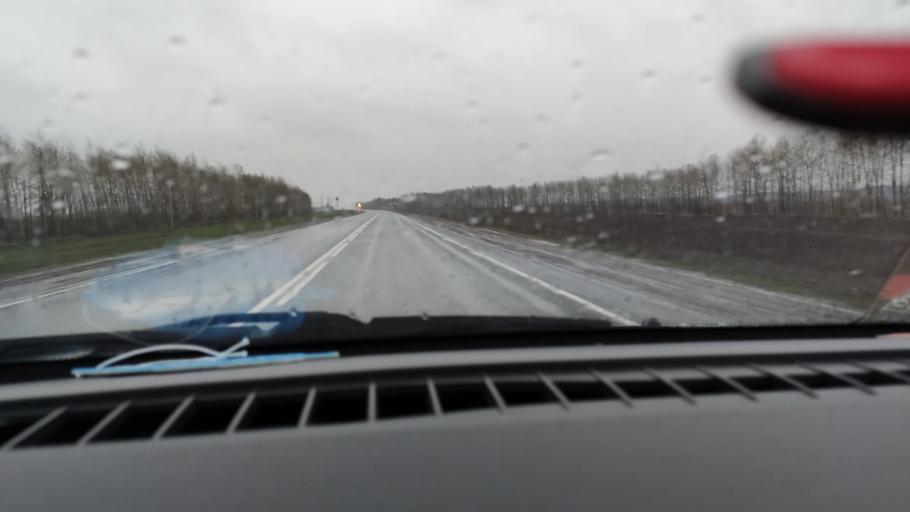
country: RU
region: Tatarstan
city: Mendeleyevsk
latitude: 55.9211
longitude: 52.2746
